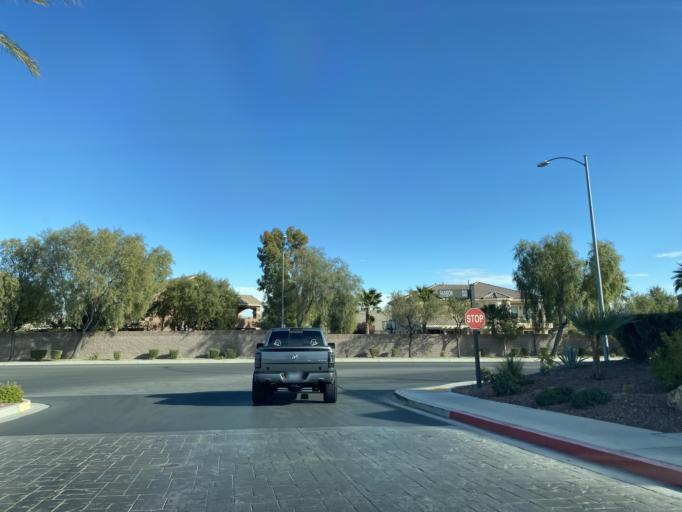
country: US
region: Nevada
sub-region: Clark County
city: North Las Vegas
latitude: 36.3125
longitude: -115.2426
